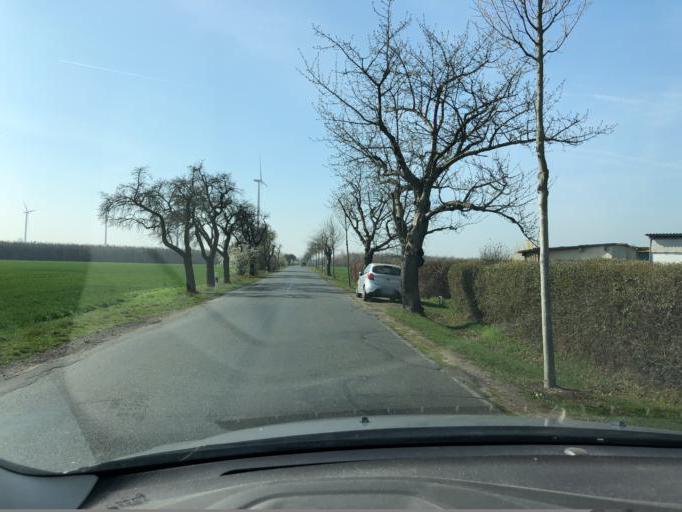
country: DE
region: Saxony
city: Krostitz
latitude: 51.4182
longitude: 12.4423
